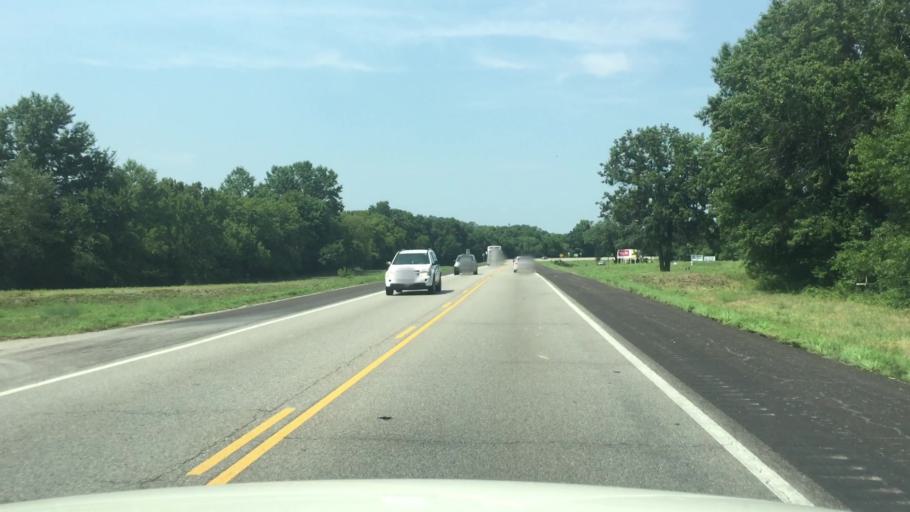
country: US
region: Kansas
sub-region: Crawford County
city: Pittsburg
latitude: 37.4044
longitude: -94.7232
